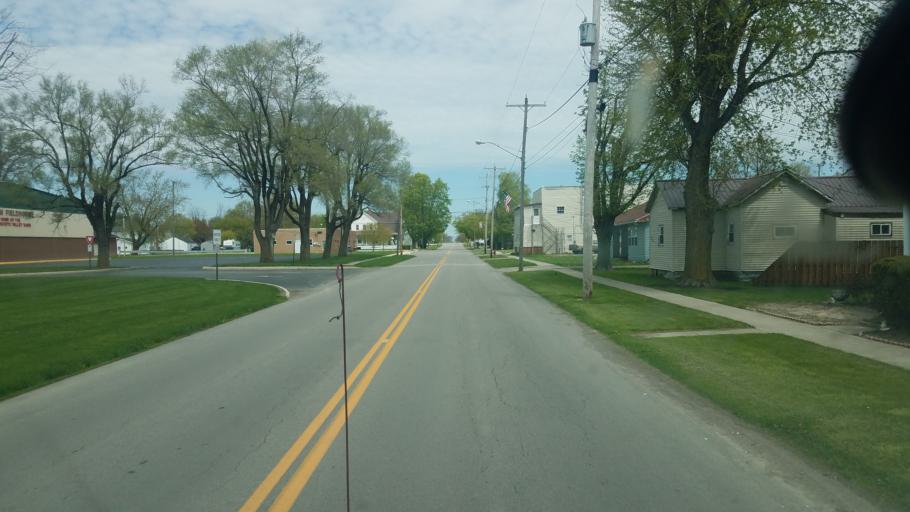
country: US
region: Ohio
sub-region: Hardin County
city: Ada
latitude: 40.6916
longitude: -83.7853
